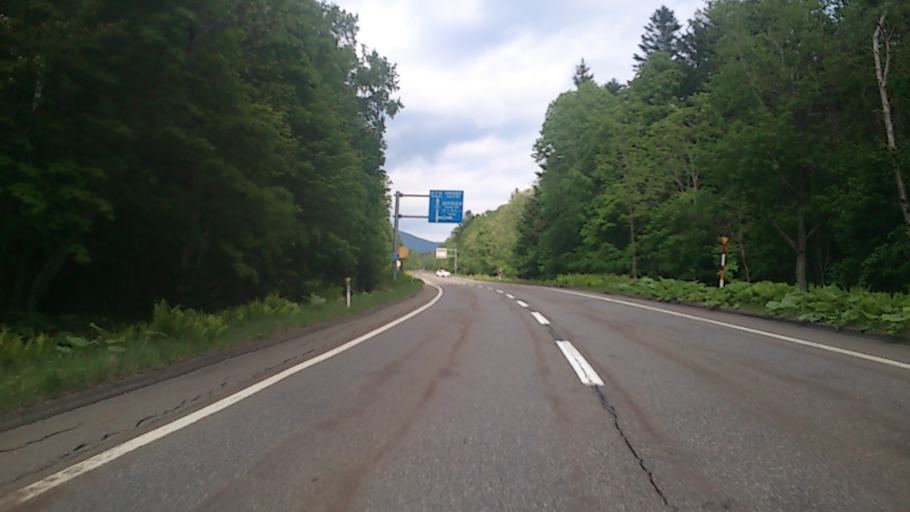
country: JP
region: Hokkaido
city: Kitami
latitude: 43.4076
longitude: 143.9523
